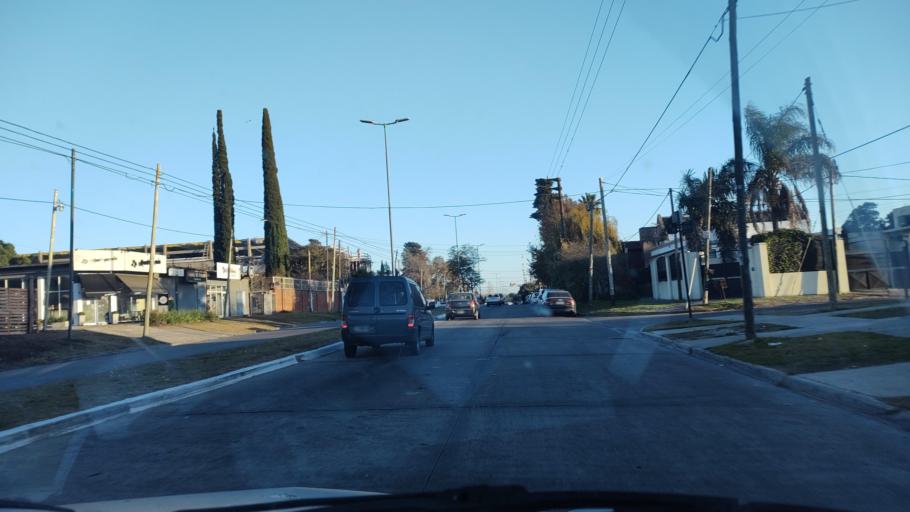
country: AR
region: Buenos Aires
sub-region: Partido de La Plata
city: La Plata
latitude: -34.8956
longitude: -58.0166
